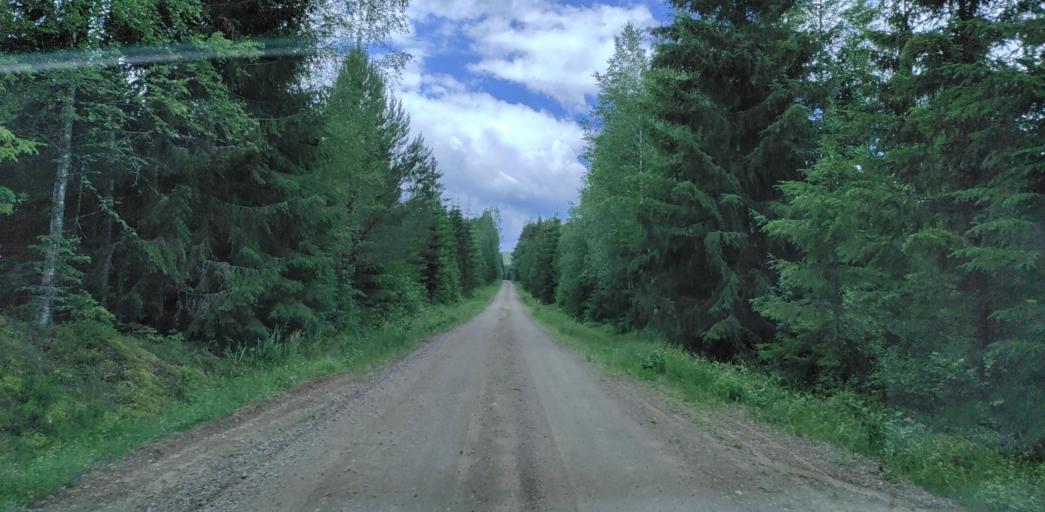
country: SE
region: Vaermland
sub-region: Hagfors Kommun
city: Ekshaerad
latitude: 60.0890
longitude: 13.4232
